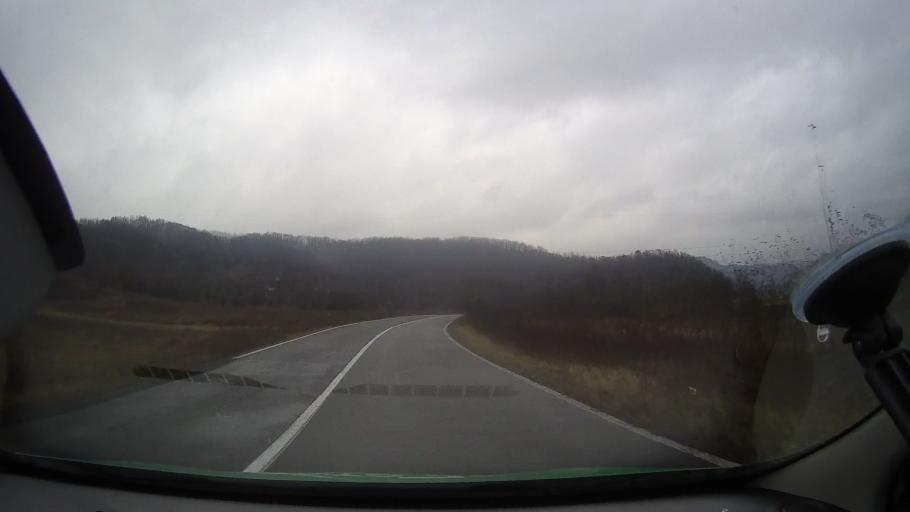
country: RO
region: Arad
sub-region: Comuna Gurahont
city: Gurahont
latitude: 46.2857
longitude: 22.3811
